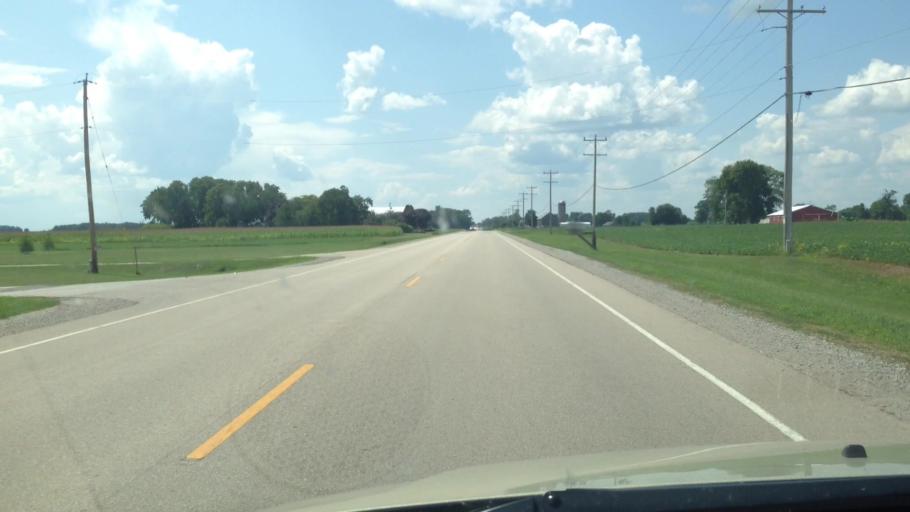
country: US
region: Wisconsin
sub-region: Brown County
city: Pulaski
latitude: 44.6731
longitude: -88.2705
